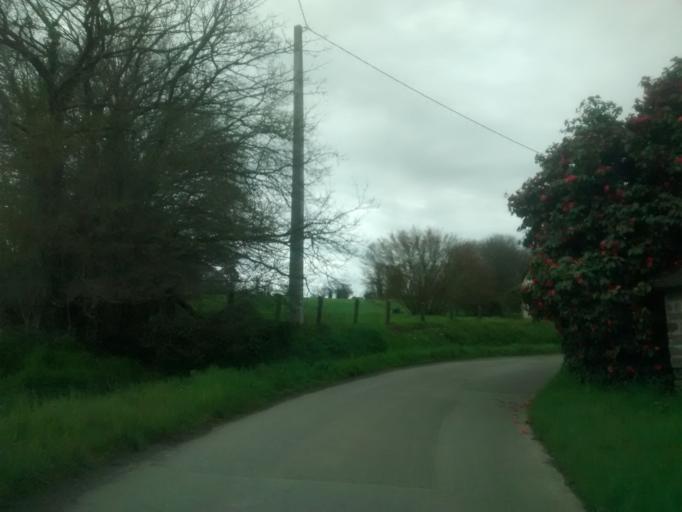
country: FR
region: Brittany
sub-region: Departement d'Ille-et-Vilaine
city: Gosne
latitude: 48.2463
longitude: -1.4786
